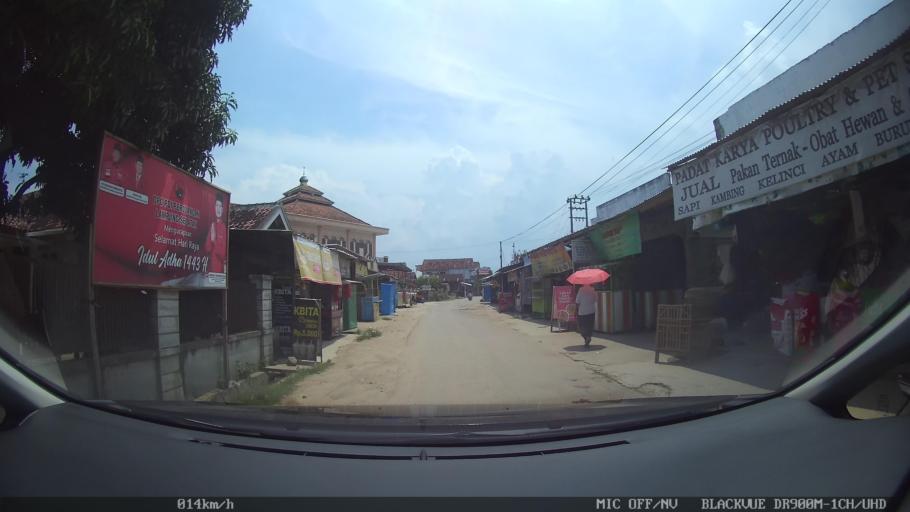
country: ID
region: Lampung
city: Natar
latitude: -5.3162
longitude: 105.2018
